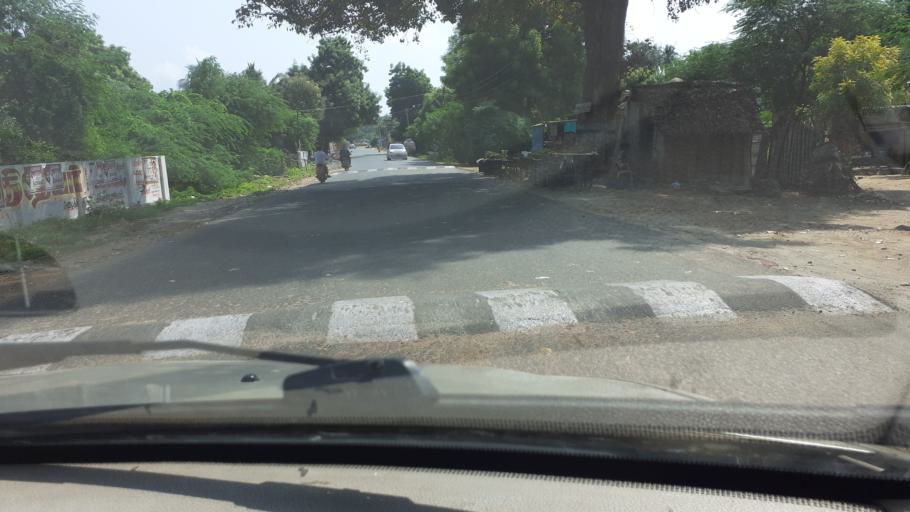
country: IN
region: Tamil Nadu
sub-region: Thoothukkudi
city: Srivaikuntam
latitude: 8.6330
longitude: 77.8977
